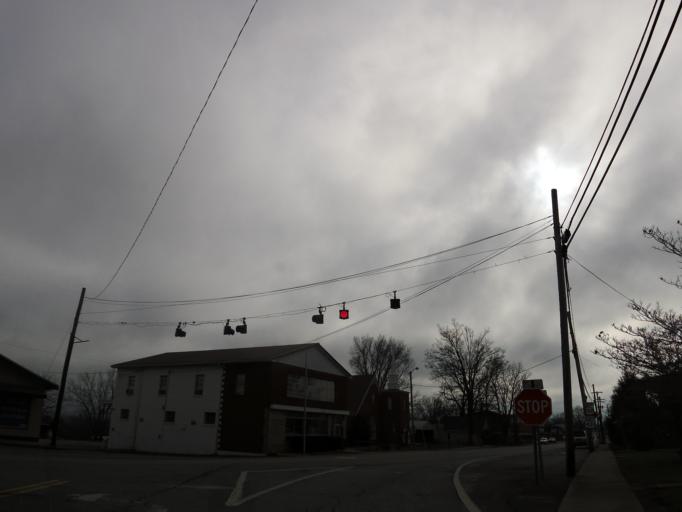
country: US
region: Kentucky
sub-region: Trimble County
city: Bedford
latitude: 38.5954
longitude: -85.3166
